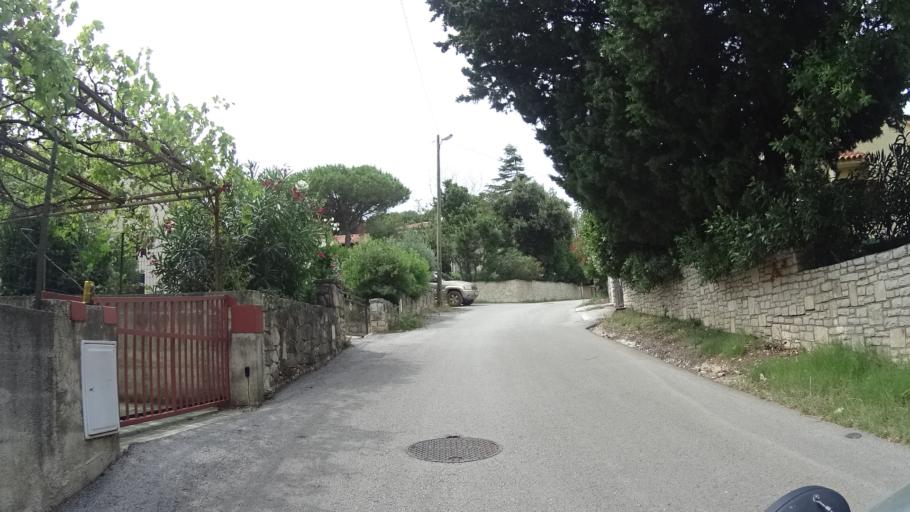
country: HR
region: Istarska
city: Medulin
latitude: 44.8015
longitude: 13.9127
